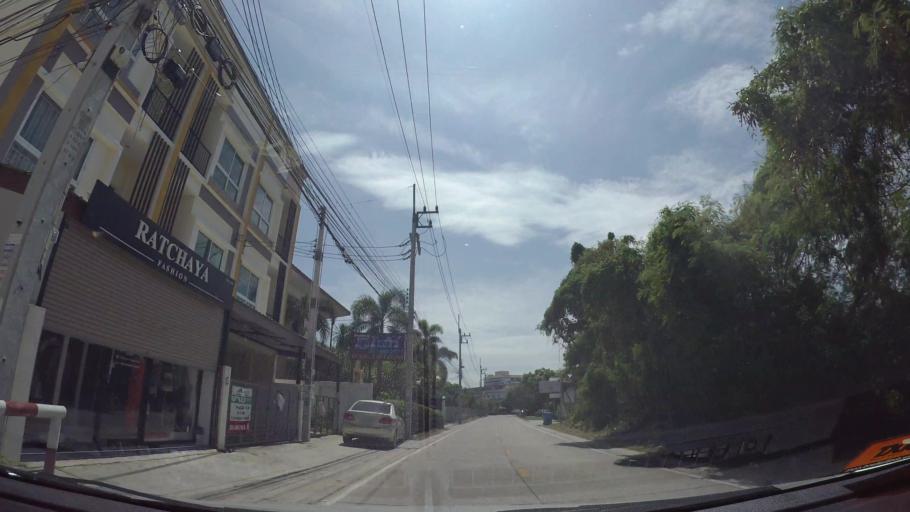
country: TH
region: Chon Buri
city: Chon Buri
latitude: 13.3213
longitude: 100.9547
